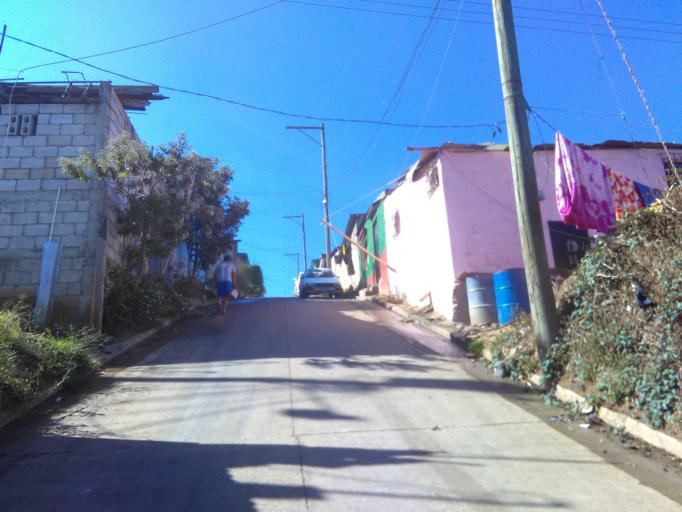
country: GT
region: Guatemala
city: Villa Canales
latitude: 14.5058
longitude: -90.5195
